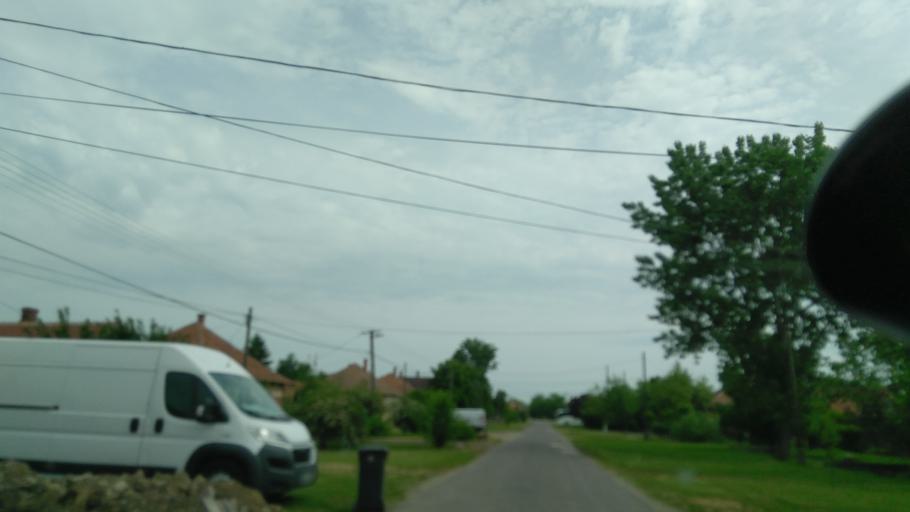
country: HU
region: Bekes
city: Szeghalom
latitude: 47.0218
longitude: 21.1687
